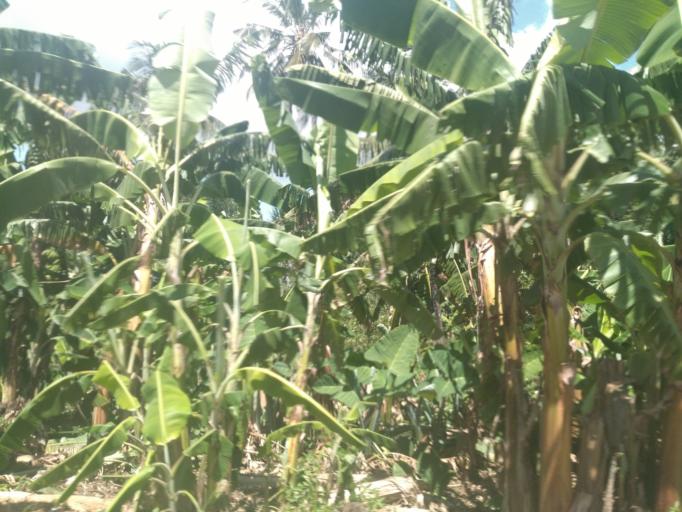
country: TZ
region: Zanzibar North
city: Gamba
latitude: -5.9365
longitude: 39.3408
